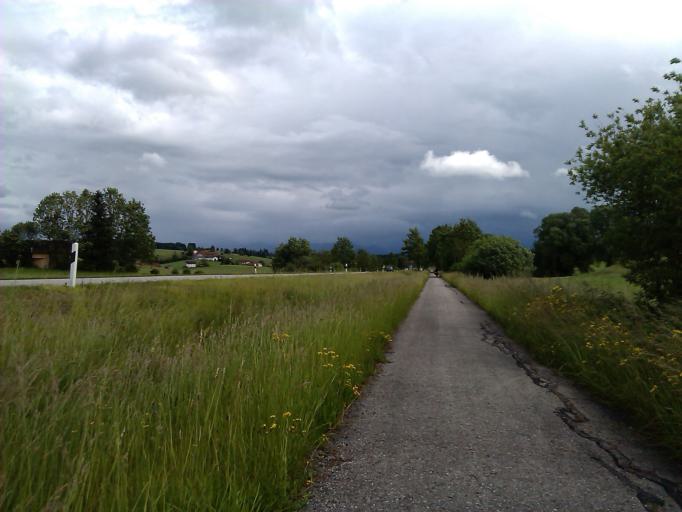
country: DE
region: Bavaria
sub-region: Swabia
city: Stotten am Auerberg
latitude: 47.7157
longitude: 10.6870
